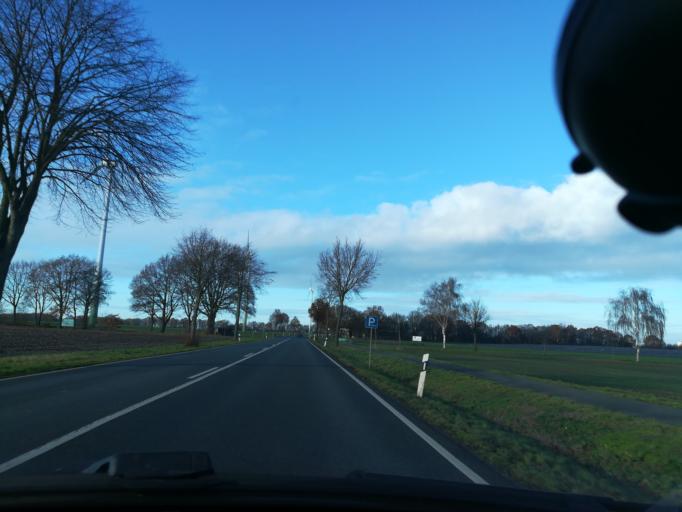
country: DE
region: Lower Saxony
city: Uchte
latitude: 52.4750
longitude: 8.8993
